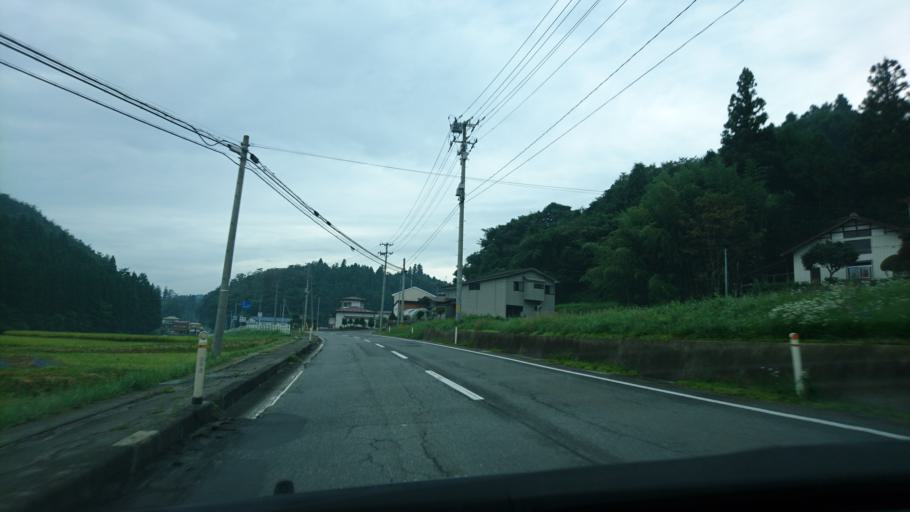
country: JP
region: Iwate
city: Ichinoseki
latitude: 39.0108
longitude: 141.2626
